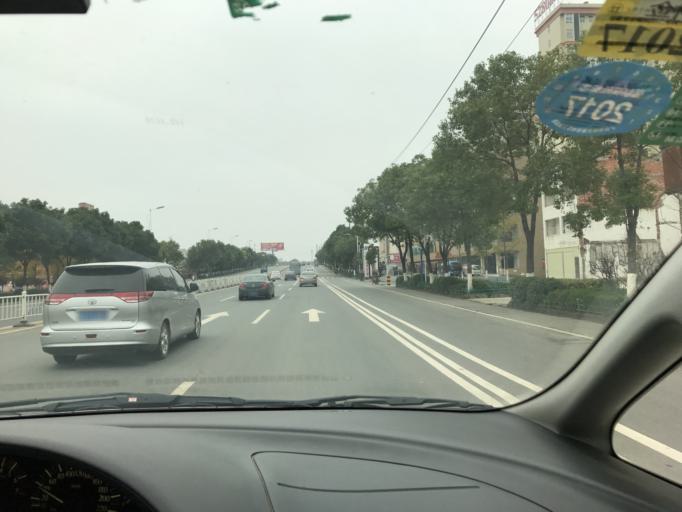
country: CN
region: Hubei
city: Anlu
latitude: 31.2508
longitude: 113.6965
